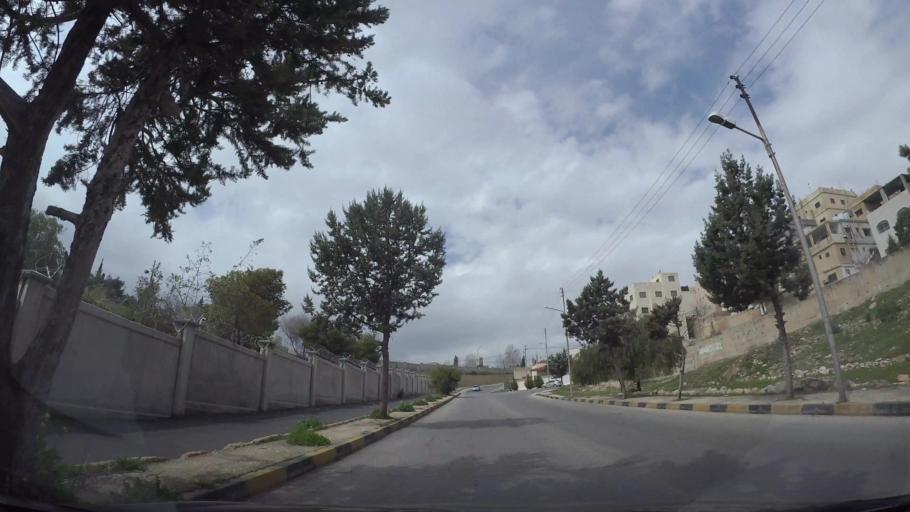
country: JO
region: Amman
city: Amman
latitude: 31.9614
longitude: 35.9497
